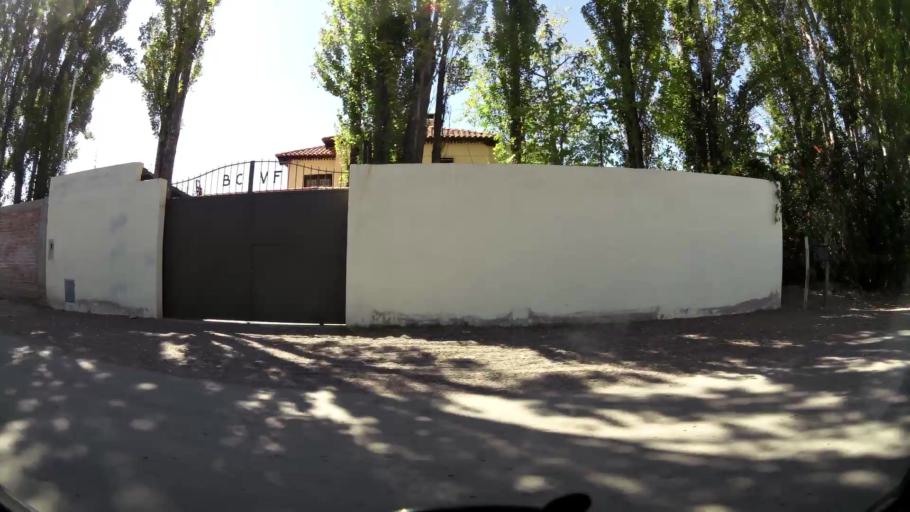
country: AR
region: Mendoza
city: Lujan de Cuyo
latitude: -32.9850
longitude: -68.8578
